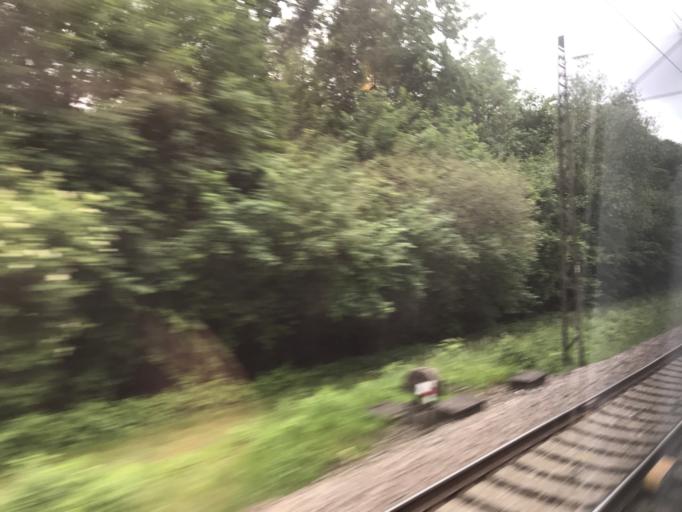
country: DE
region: Bavaria
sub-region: Swabia
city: Guenzburg
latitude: 48.4652
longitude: 10.2956
